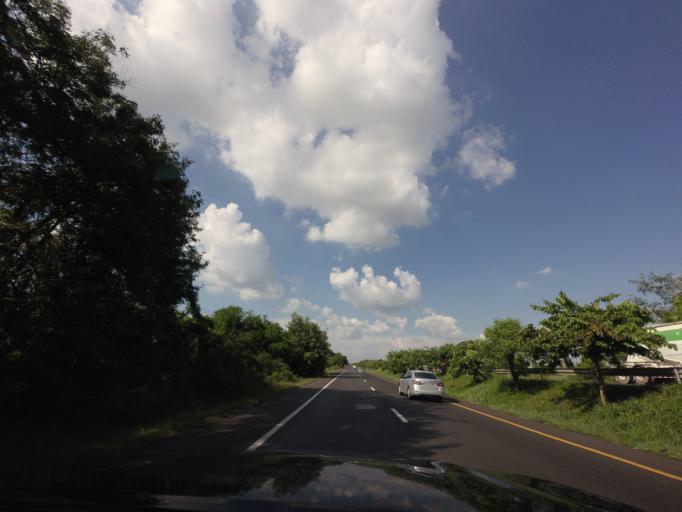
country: TH
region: Nakhon Ratchasima
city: Bua Lai
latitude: 15.6855
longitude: 102.5783
